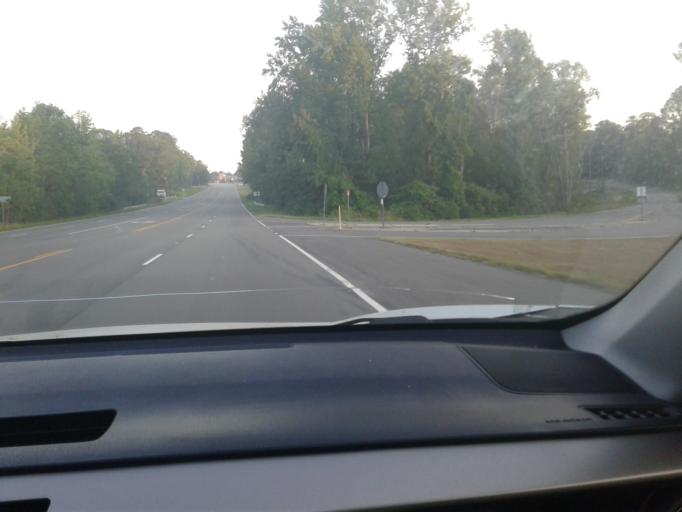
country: US
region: North Carolina
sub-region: Harnett County
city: Buies Creek
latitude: 35.3991
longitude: -78.7338
